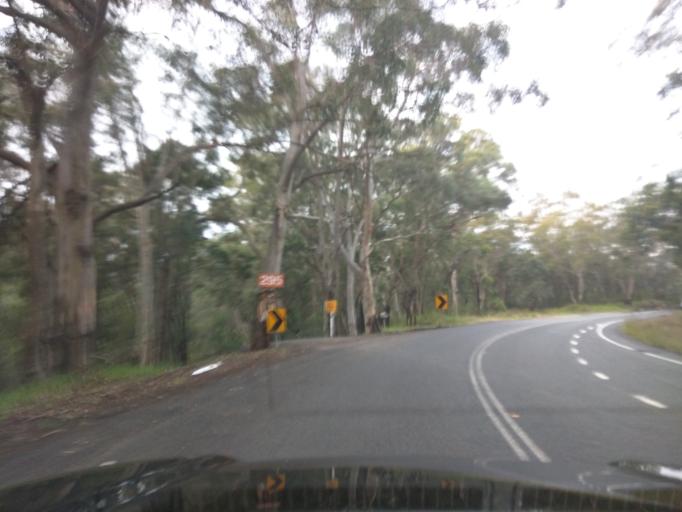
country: AU
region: New South Wales
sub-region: Wollondilly
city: Douglas Park
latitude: -34.2299
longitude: 150.7396
